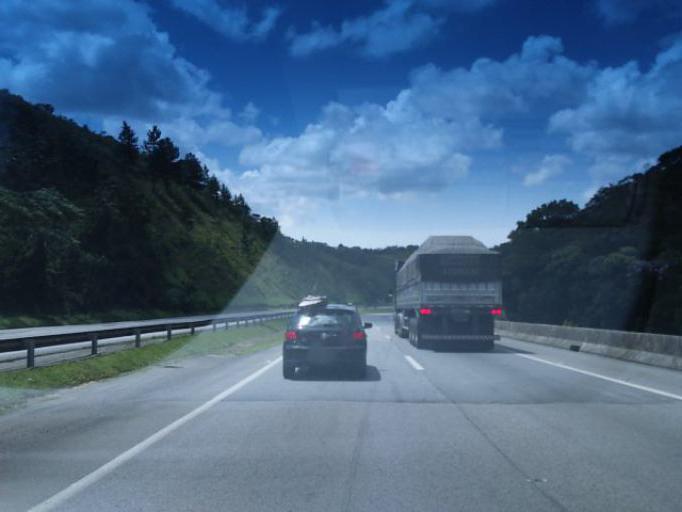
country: BR
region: Sao Paulo
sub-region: Juquitiba
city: Juquitiba
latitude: -23.9912
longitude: -47.1480
